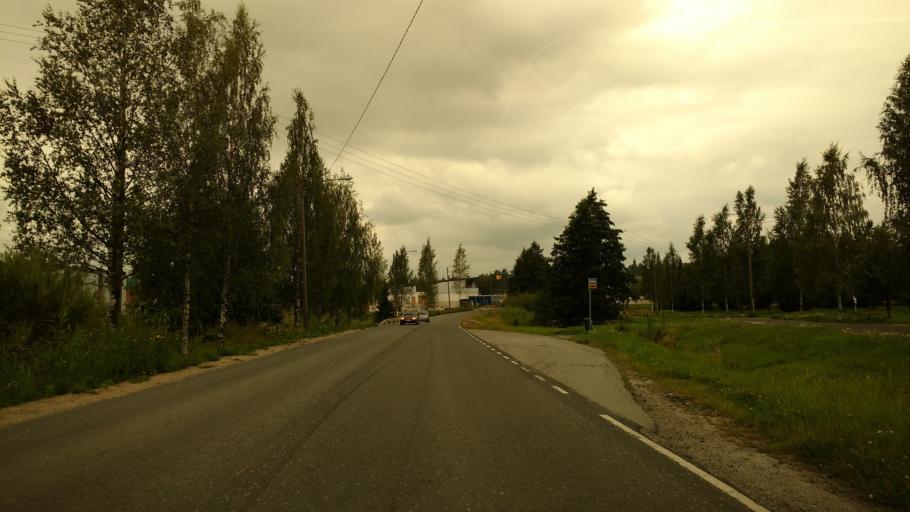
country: FI
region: Varsinais-Suomi
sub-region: Salo
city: Halikko
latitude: 60.3950
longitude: 23.0868
